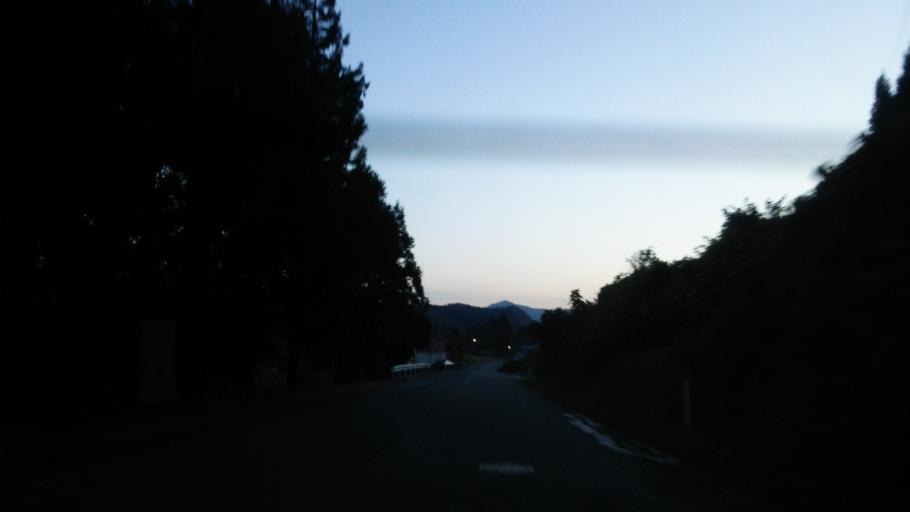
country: JP
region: Fukushima
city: Kitakata
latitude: 37.5281
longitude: 139.7137
